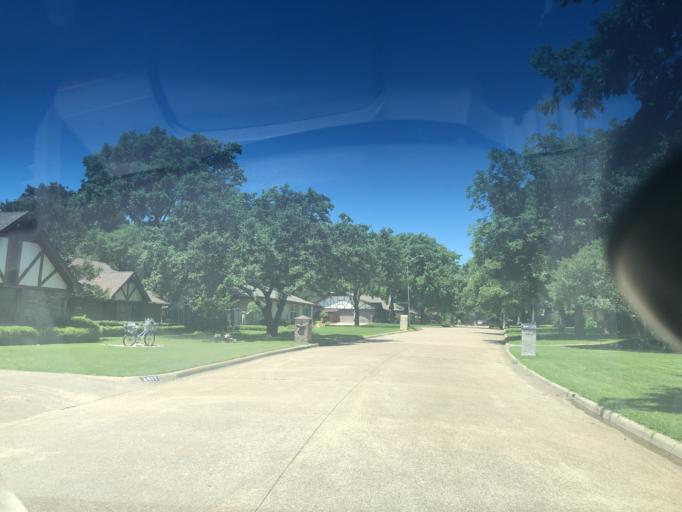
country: US
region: Texas
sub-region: Dallas County
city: Grand Prairie
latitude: 32.7779
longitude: -97.0389
